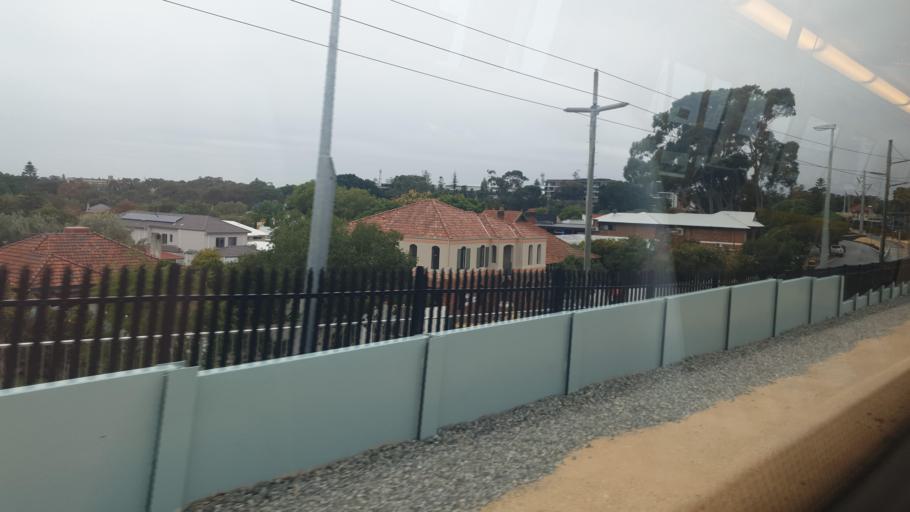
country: AU
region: Western Australia
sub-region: Claremont
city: Claremont
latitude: -31.9815
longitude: 115.7777
